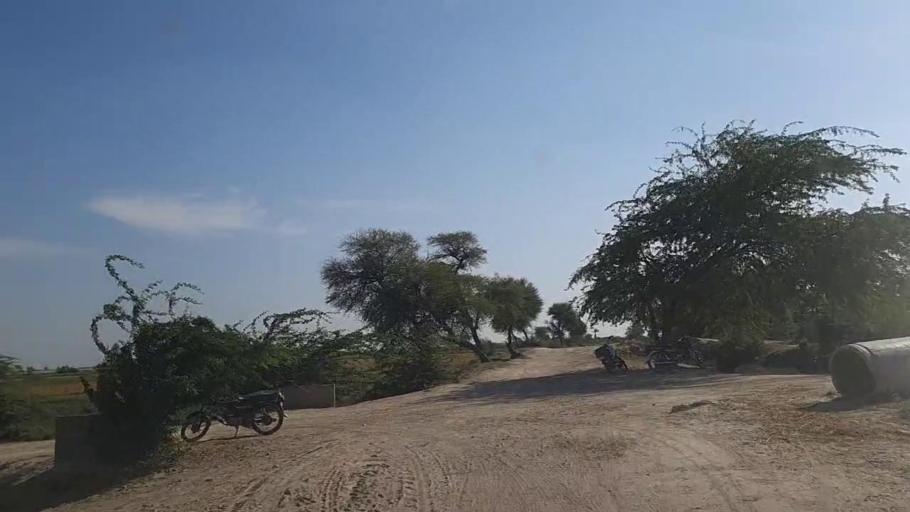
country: PK
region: Sindh
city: Bulri
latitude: 24.8555
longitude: 68.2893
